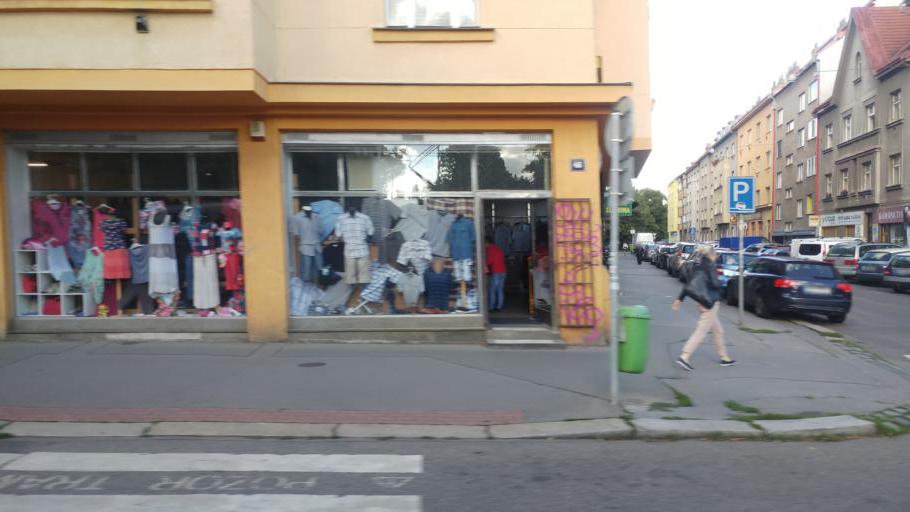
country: CZ
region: Praha
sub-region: Praha 8
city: Liben
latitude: 50.0749
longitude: 14.4901
